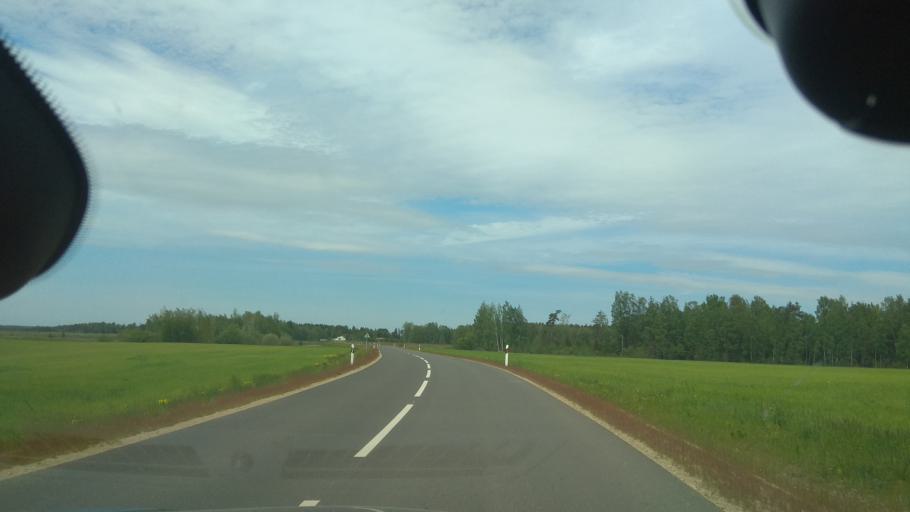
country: LT
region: Vilnius County
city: Ukmerge
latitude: 55.1245
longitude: 24.6083
